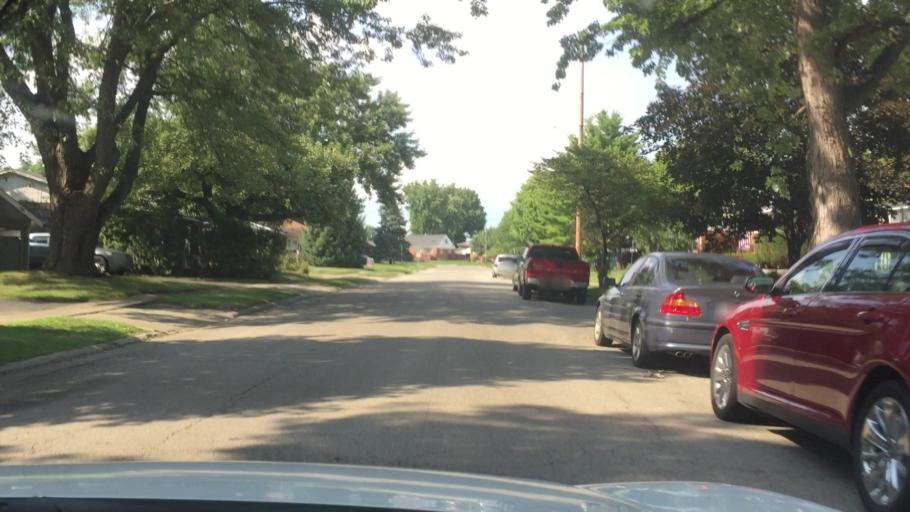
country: US
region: Ohio
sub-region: Clark County
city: Northridge
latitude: 39.9931
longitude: -83.7781
